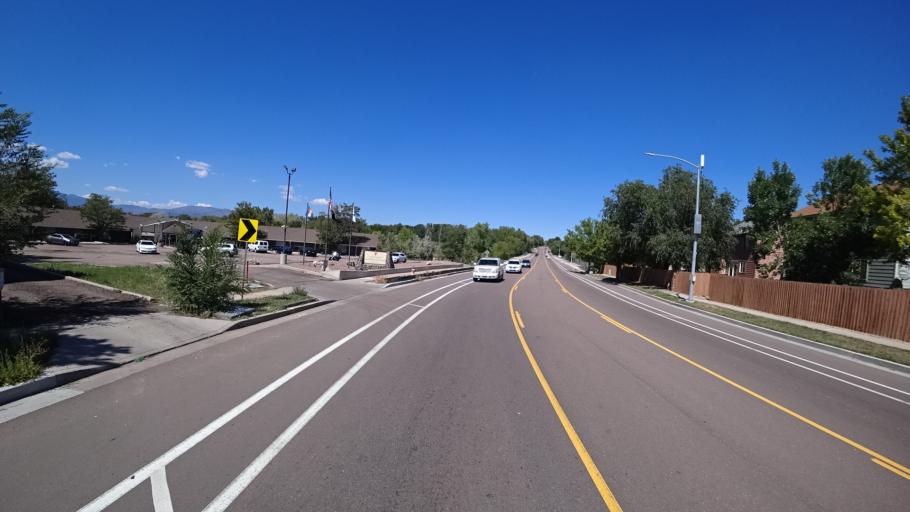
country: US
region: Colorado
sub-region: El Paso County
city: Stratmoor
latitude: 38.8188
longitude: -104.7678
